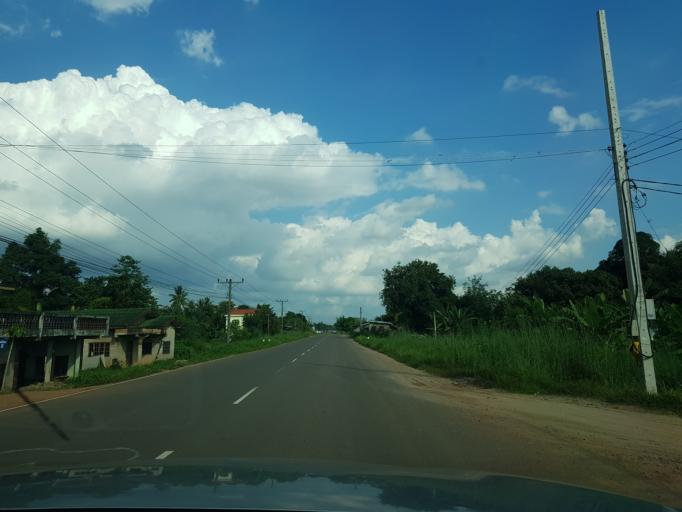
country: TH
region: Nong Khai
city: Pho Tak
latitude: 17.9823
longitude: 102.4488
